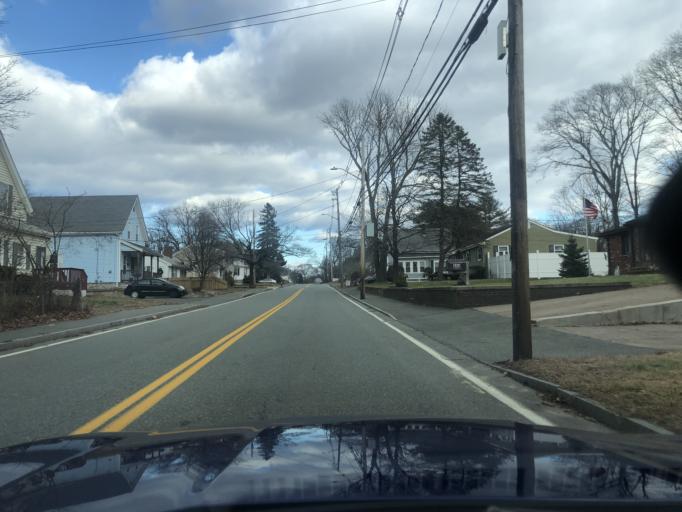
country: US
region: Massachusetts
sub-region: Plymouth County
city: Brockton
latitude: 42.1122
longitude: -71.0145
